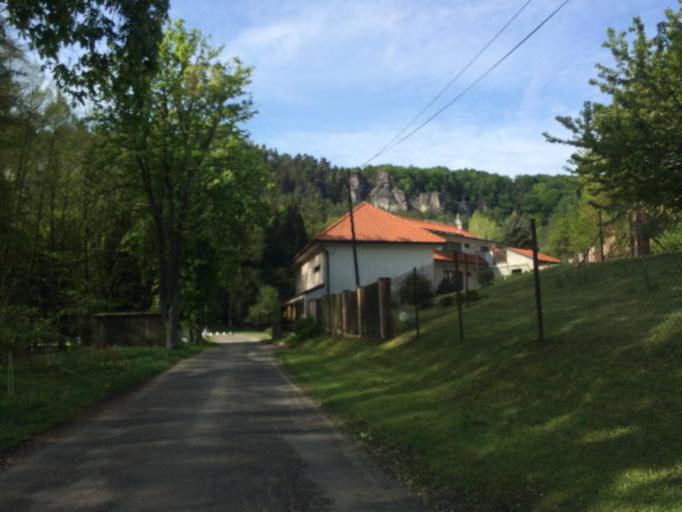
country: CZ
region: Central Bohemia
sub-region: Okres Mlada Boleslav
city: Zd'ar
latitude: 50.5281
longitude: 15.0756
